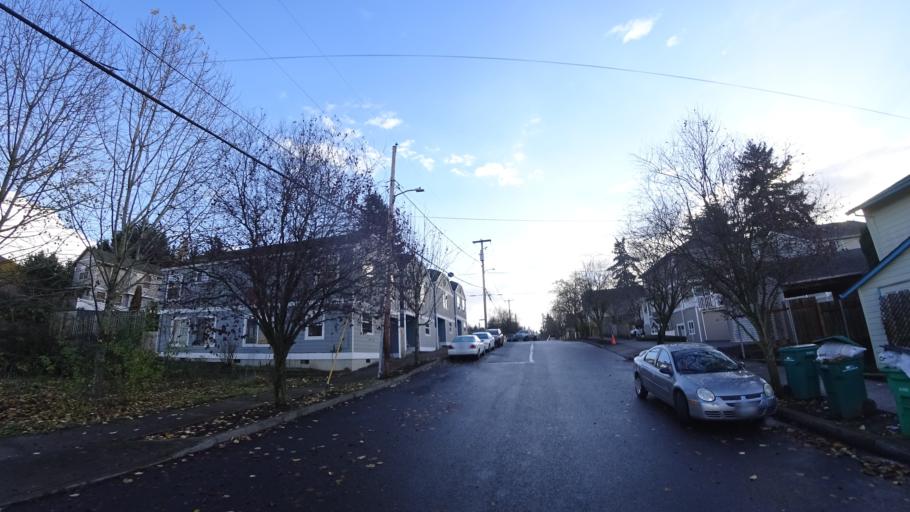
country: US
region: Oregon
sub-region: Multnomah County
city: Lents
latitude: 45.5209
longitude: -122.5404
